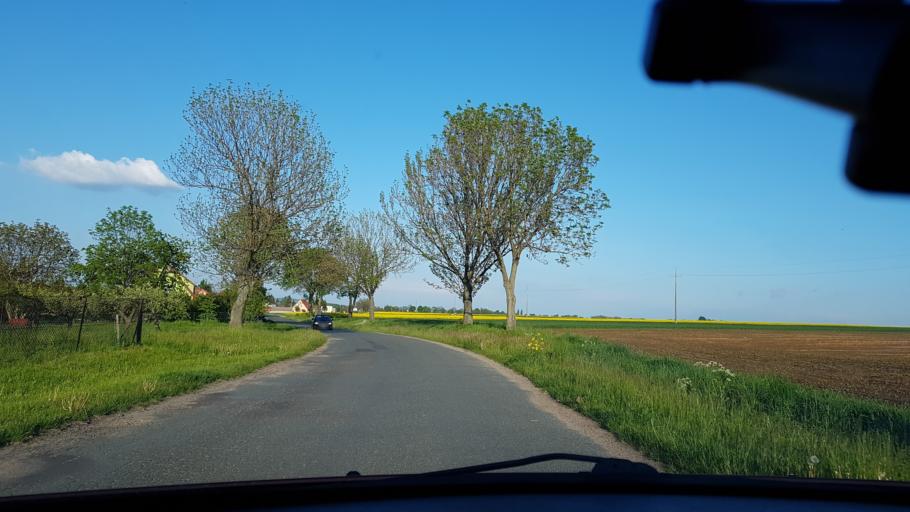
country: PL
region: Lower Silesian Voivodeship
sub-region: Powiat zabkowicki
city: Budzow
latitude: 50.6074
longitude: 16.7167
